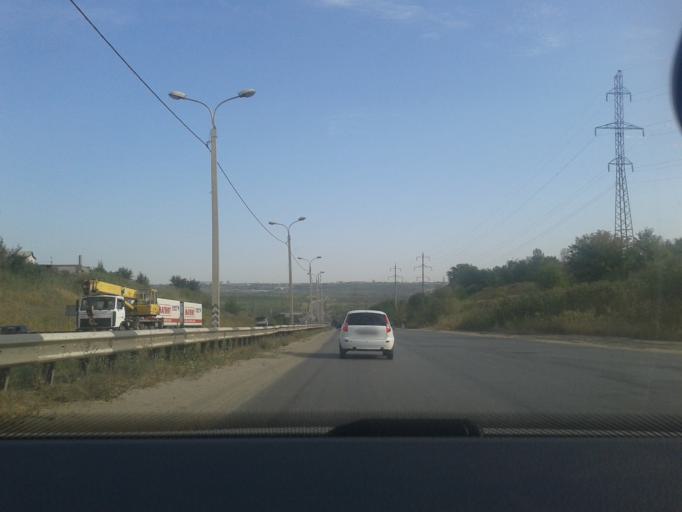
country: RU
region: Volgograd
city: Volgograd
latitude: 48.7070
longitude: 44.4413
